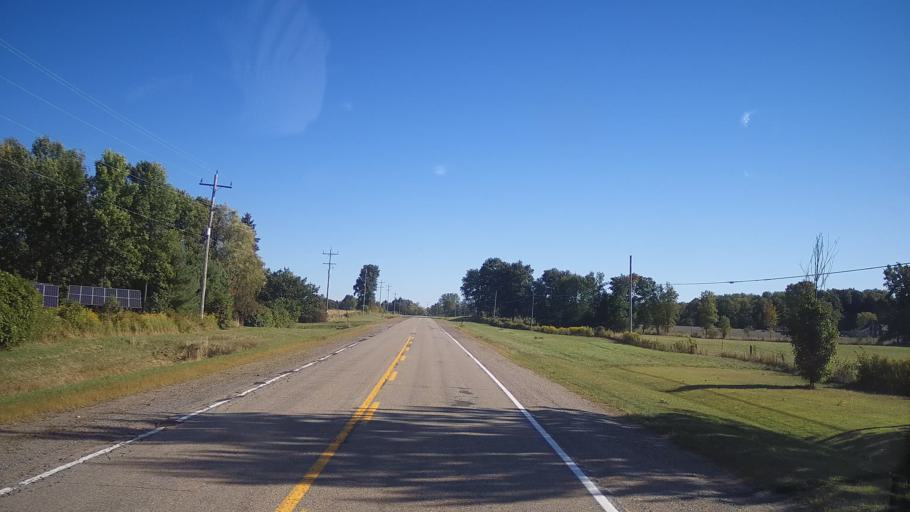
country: CA
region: Ontario
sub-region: Lanark County
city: Smiths Falls
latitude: 44.6186
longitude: -76.0466
